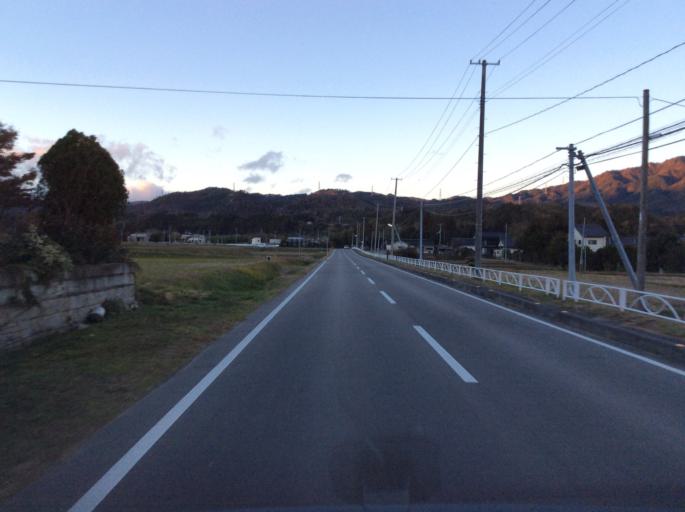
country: JP
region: Fukushima
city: Iwaki
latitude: 37.1302
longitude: 140.8512
